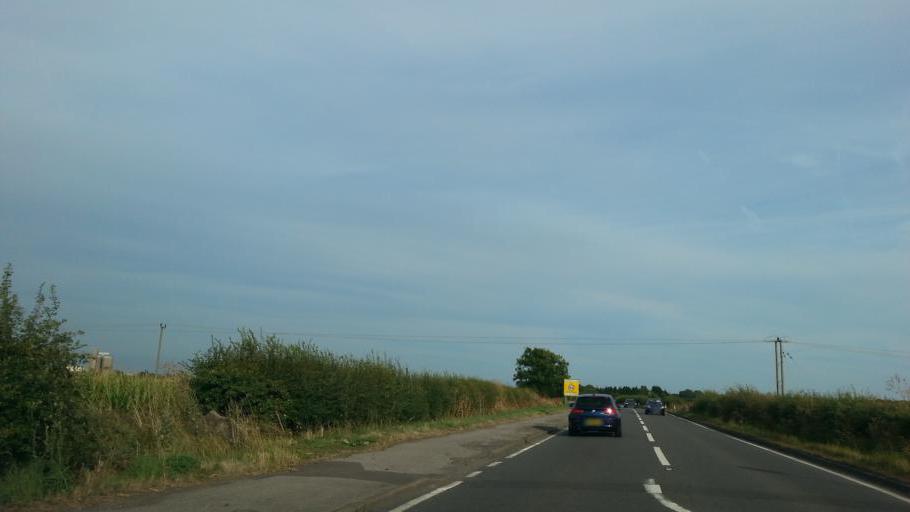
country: GB
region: England
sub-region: Nottinghamshire
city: Newark on Trent
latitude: 53.0883
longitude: -0.8395
